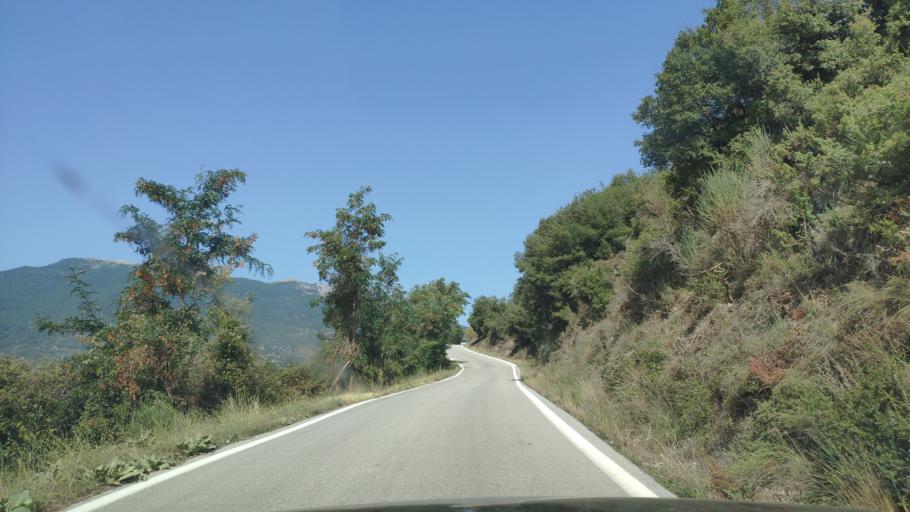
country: GR
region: West Greece
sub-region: Nomos Achaias
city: Aiyira
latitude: 37.9189
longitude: 22.3313
